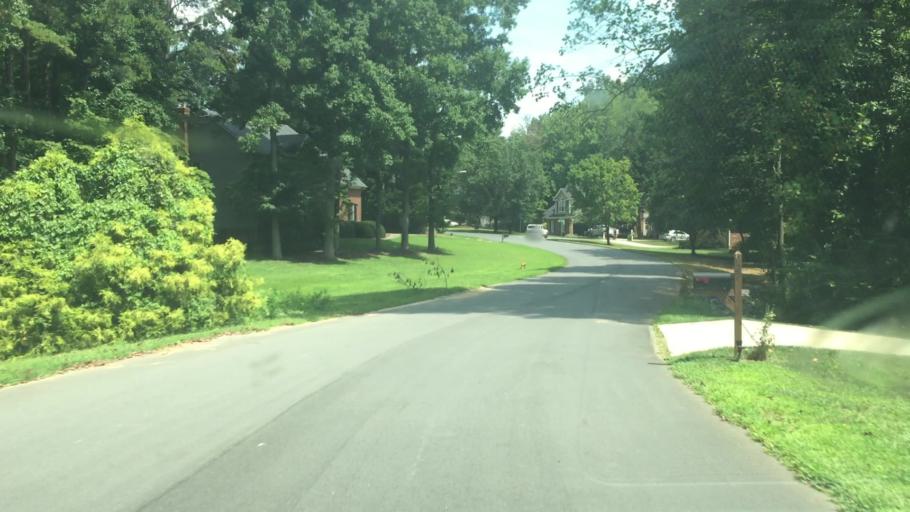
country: US
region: North Carolina
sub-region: Iredell County
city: Mooresville
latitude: 35.5526
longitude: -80.7977
